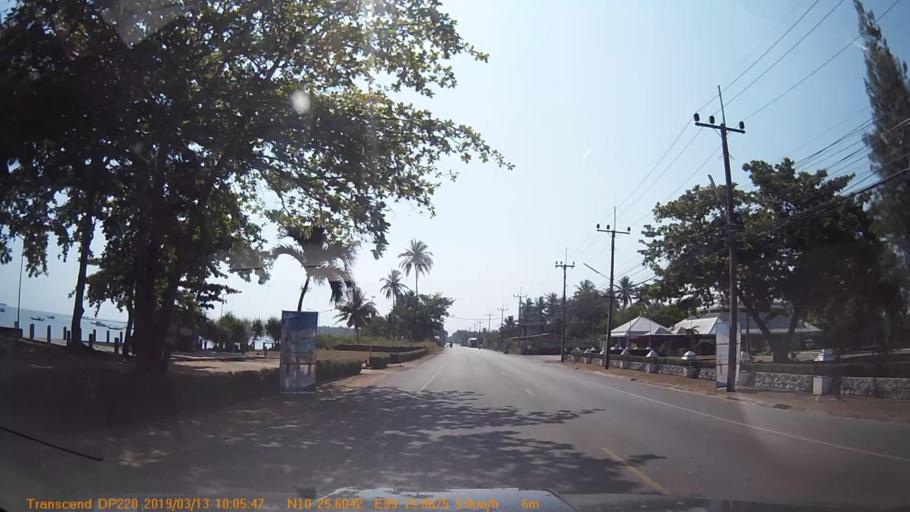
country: TH
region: Chumphon
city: Chumphon
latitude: 10.4266
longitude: 99.2647
